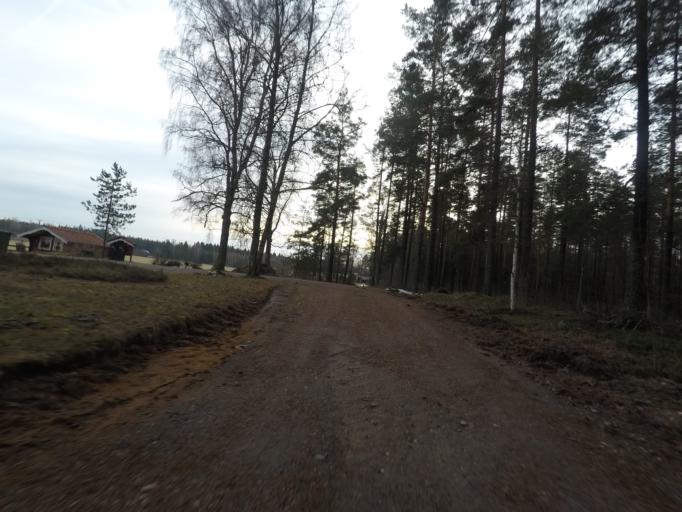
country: SE
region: Vaestmanland
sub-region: Kungsors Kommun
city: Kungsoer
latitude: 59.3429
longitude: 16.1189
